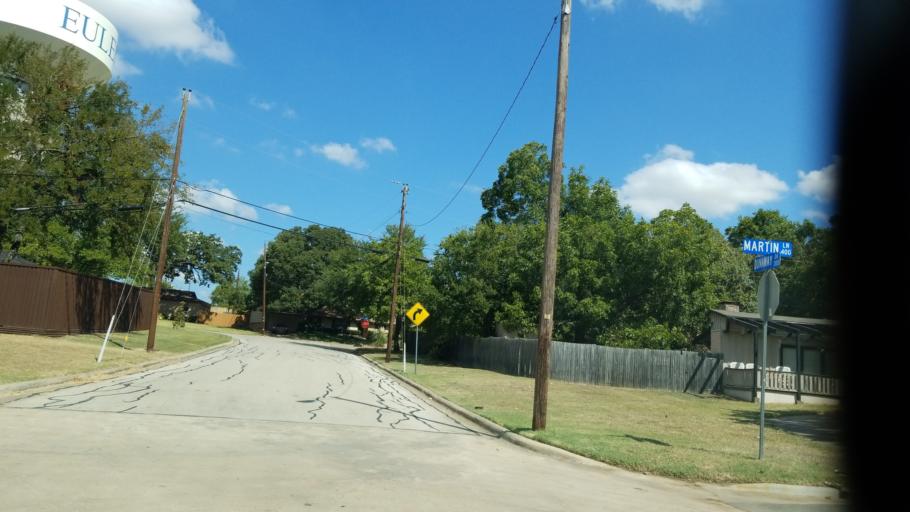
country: US
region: Texas
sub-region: Tarrant County
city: Euless
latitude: 32.8341
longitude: -97.0778
